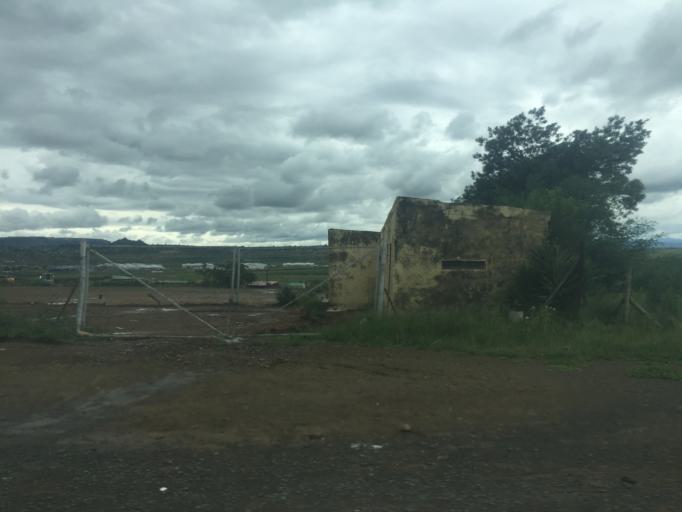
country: LS
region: Maseru
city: Maseru
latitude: -29.3850
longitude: 27.4706
